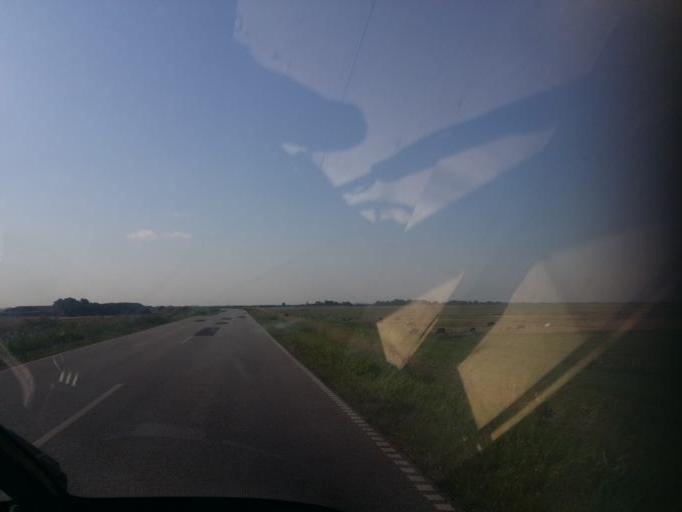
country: DE
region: Schleswig-Holstein
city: Rodenas
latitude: 54.9407
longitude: 8.7108
